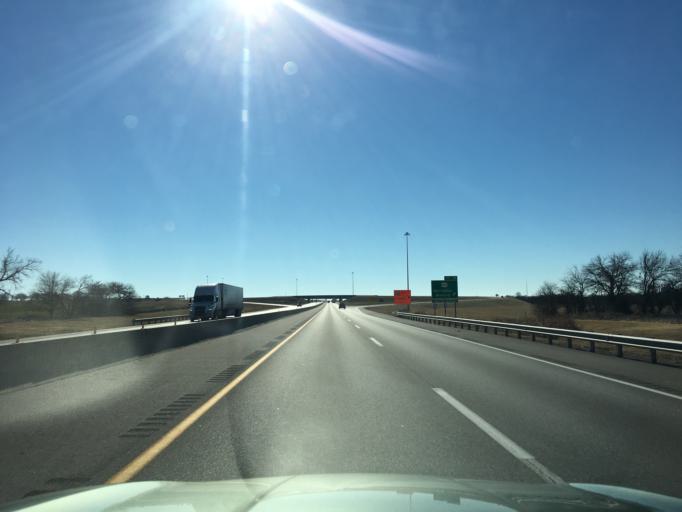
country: US
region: Kansas
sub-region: Sumner County
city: Wellington
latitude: 37.2844
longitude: -97.3403
